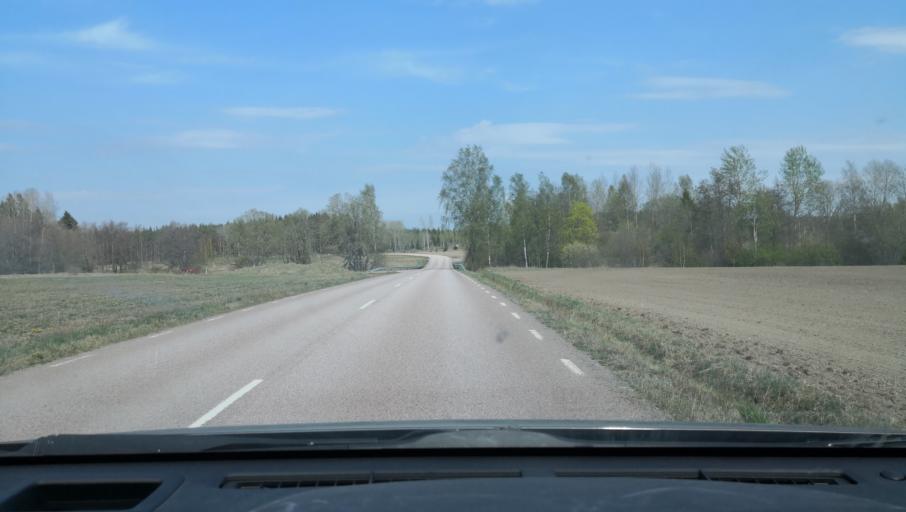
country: SE
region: Vaestmanland
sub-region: Vasteras
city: Skultuna
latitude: 59.7444
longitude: 16.4113
